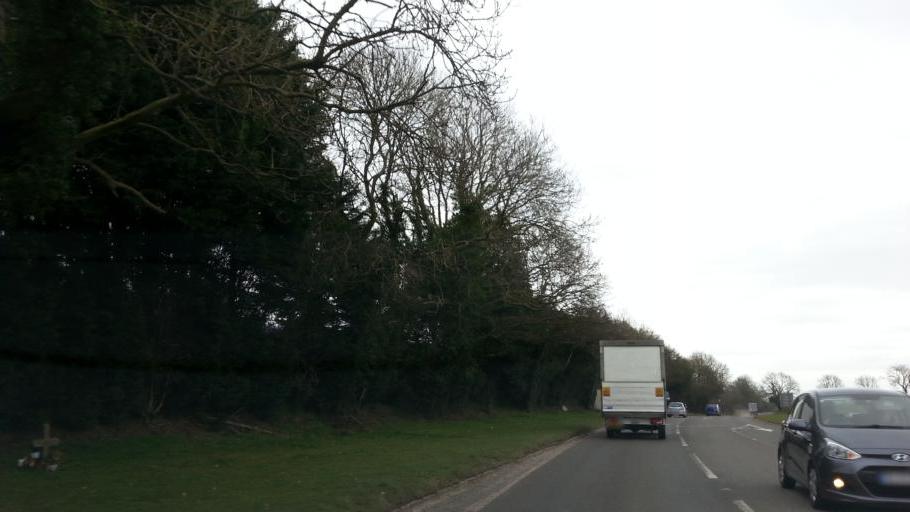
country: GB
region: England
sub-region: Staffordshire
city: Stone
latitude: 52.8868
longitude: -2.1215
